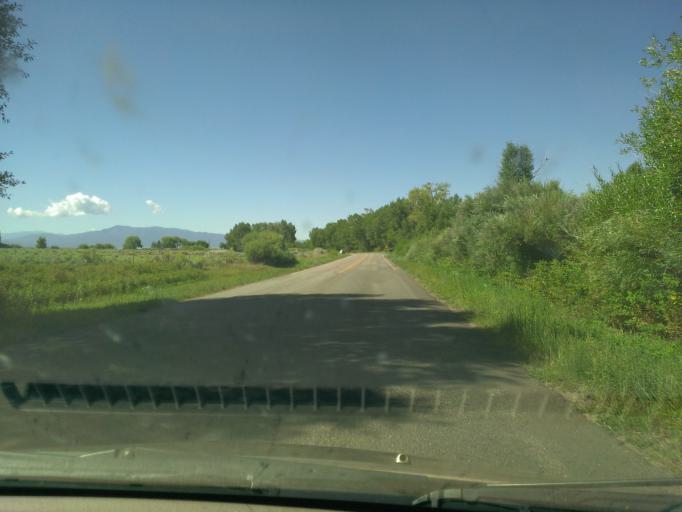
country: US
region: New Mexico
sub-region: Taos County
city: Arroyo Seco
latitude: 36.5050
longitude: -105.5881
